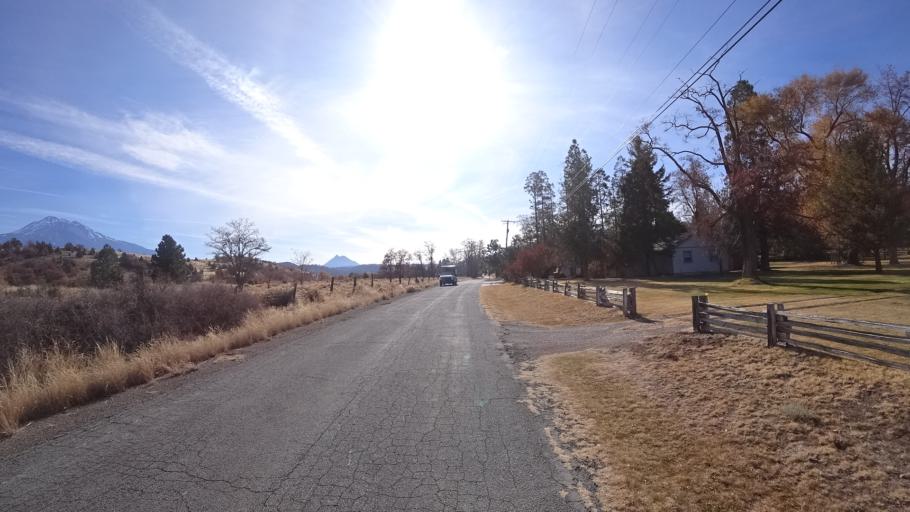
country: US
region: California
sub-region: Siskiyou County
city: Weed
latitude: 41.4810
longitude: -122.4425
